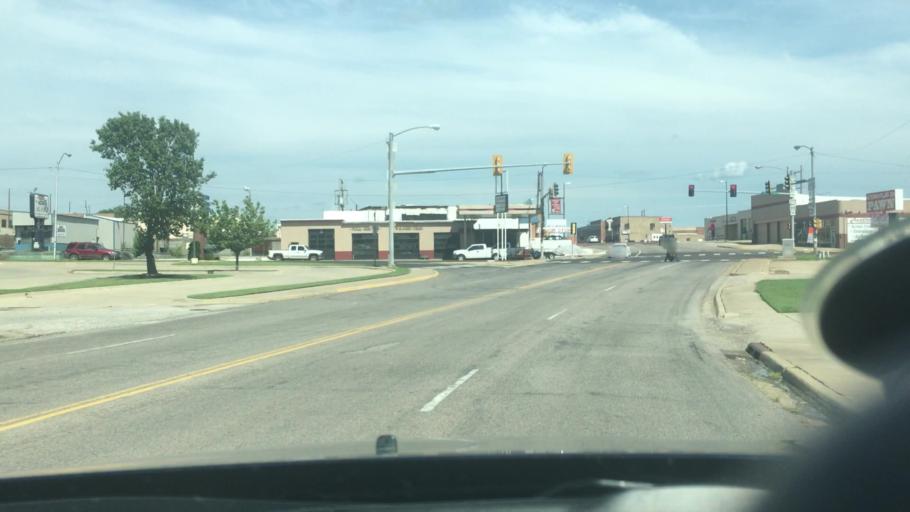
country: US
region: Oklahoma
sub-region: Seminole County
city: Seminole
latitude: 35.2247
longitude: -96.6720
